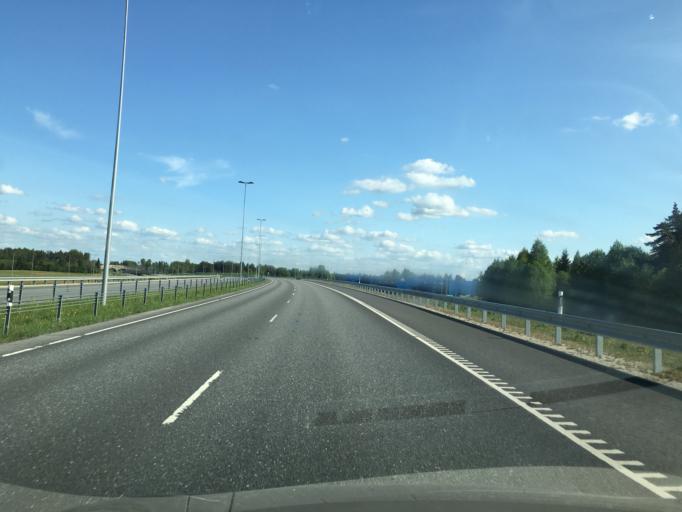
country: EE
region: Harju
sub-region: Rae vald
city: Vaida
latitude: 59.1937
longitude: 25.0456
